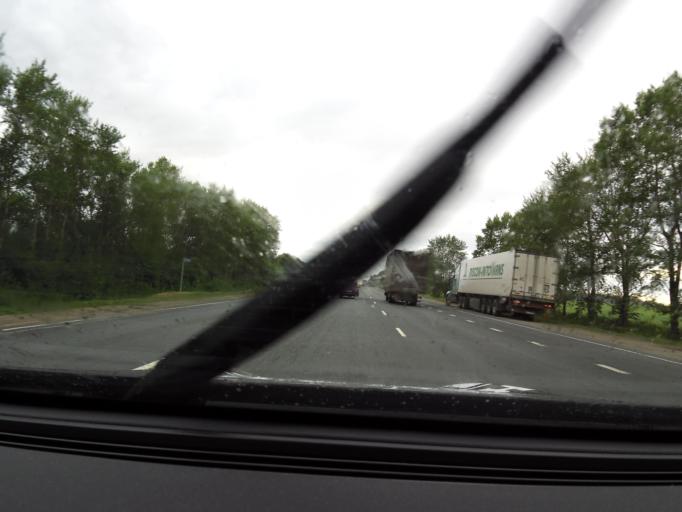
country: RU
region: Chuvashia
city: Yantikovo
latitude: 55.7931
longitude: 47.8051
